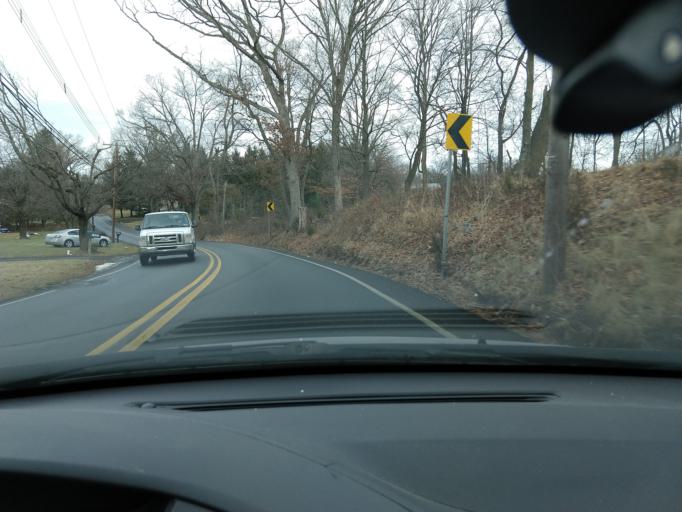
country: US
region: Pennsylvania
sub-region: Chester County
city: South Pottstown
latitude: 40.2057
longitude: -75.6669
